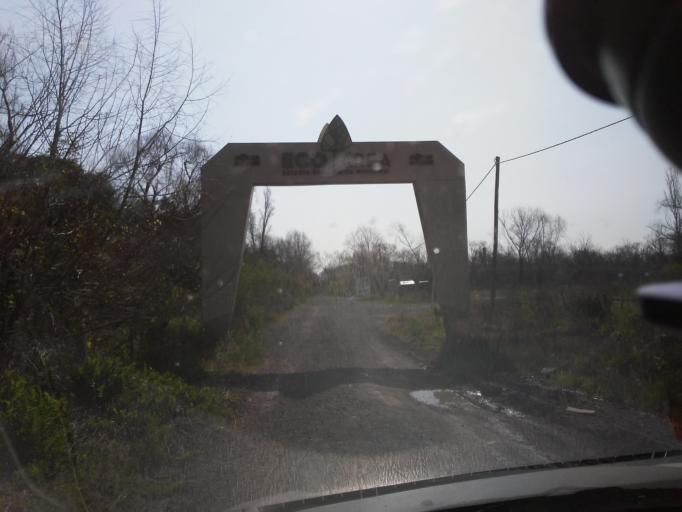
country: AR
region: Buenos Aires
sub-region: Partido de Avellaneda
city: Avellaneda
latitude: -34.6670
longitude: -58.3153
